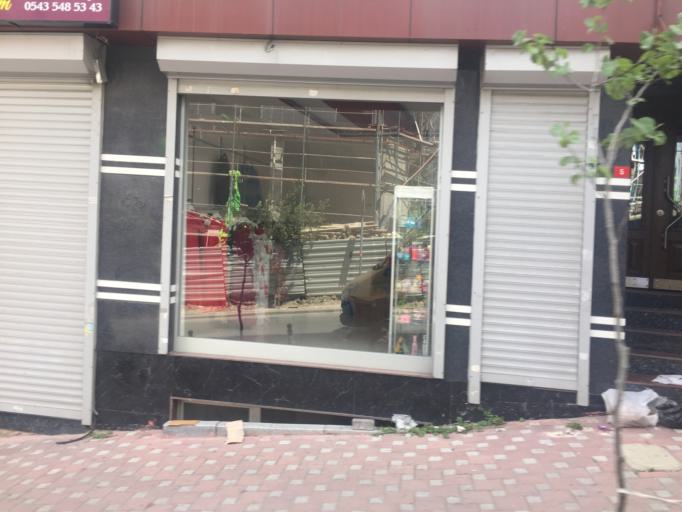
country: TR
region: Istanbul
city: Esenler
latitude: 41.0529
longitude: 28.9040
